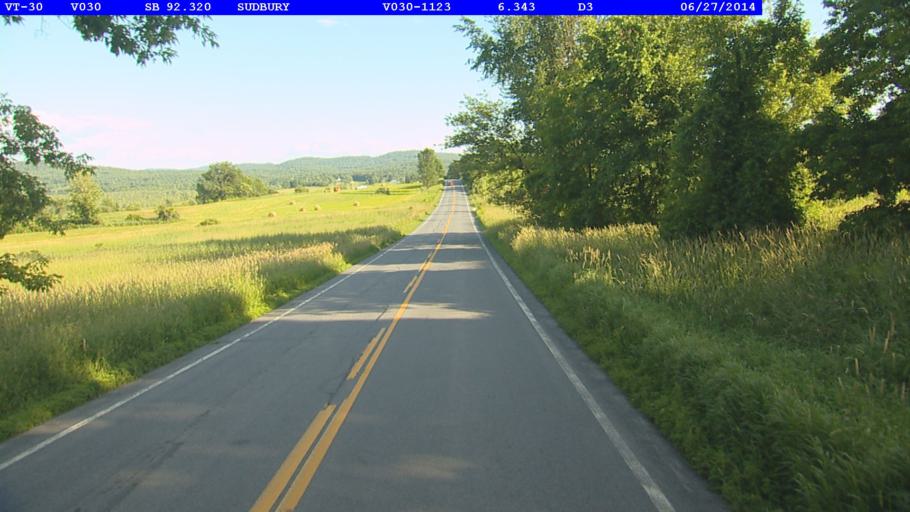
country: US
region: Vermont
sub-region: Rutland County
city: Brandon
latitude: 43.8375
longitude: -73.1946
